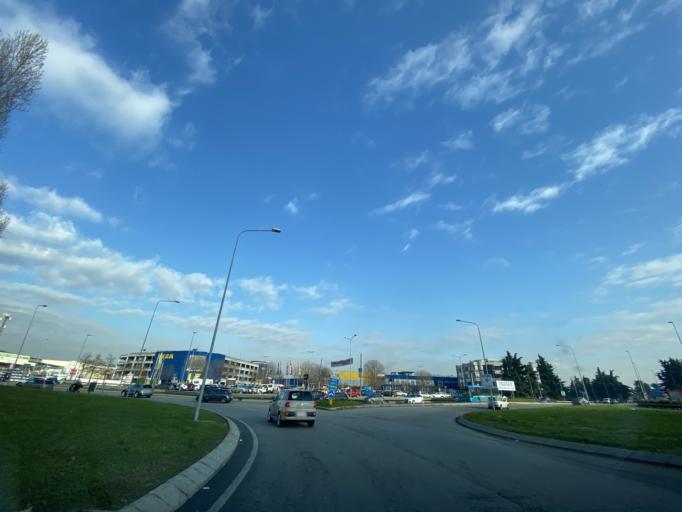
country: IT
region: Lombardy
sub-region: Citta metropolitana di Milano
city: Carugate
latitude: 45.5481
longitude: 9.3296
